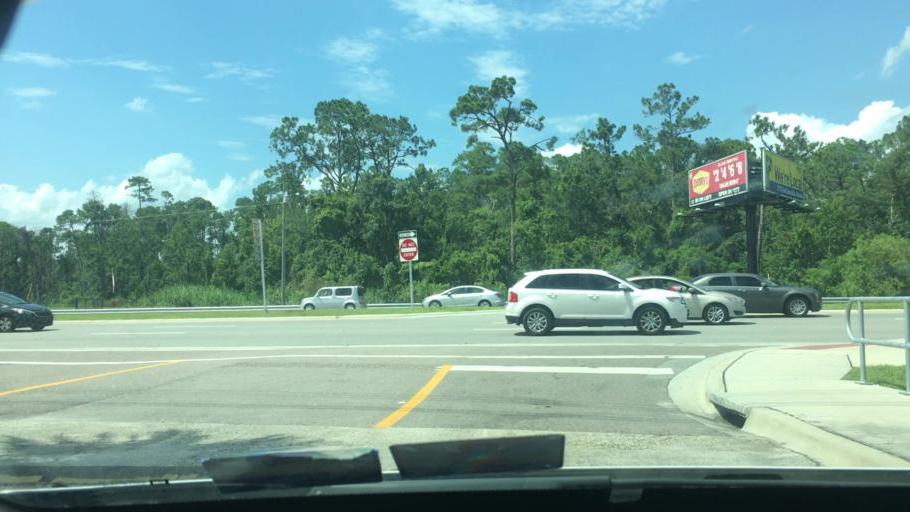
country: US
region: Florida
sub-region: Orange County
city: Alafaya
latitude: 28.5672
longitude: -81.2138
